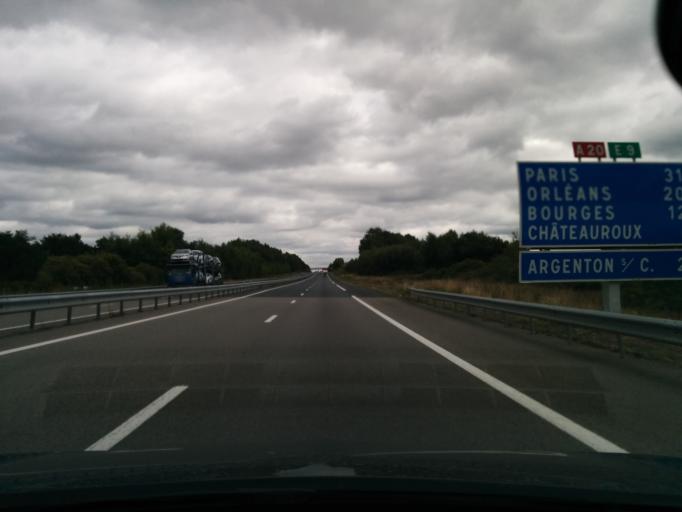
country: FR
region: Limousin
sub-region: Departement de la Haute-Vienne
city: Saint-Sulpice-les-Feuilles
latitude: 46.3645
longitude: 1.4354
